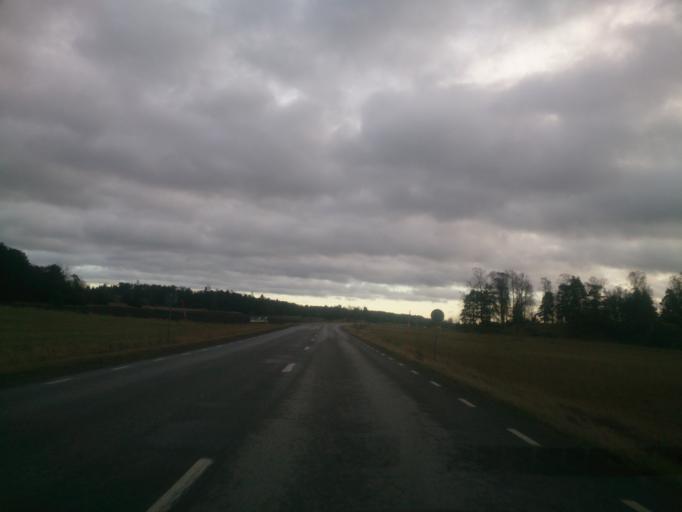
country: SE
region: OEstergoetland
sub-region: Norrkopings Kommun
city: Krokek
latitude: 58.5767
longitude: 16.5726
